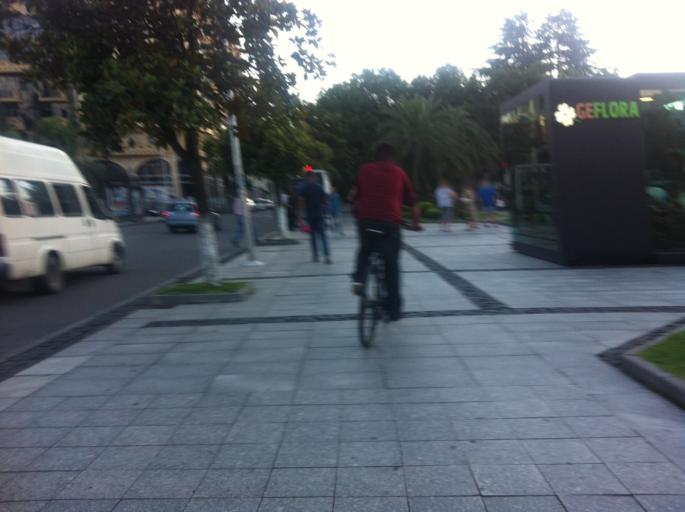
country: GE
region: Ajaria
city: Batumi
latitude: 41.6490
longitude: 41.6353
